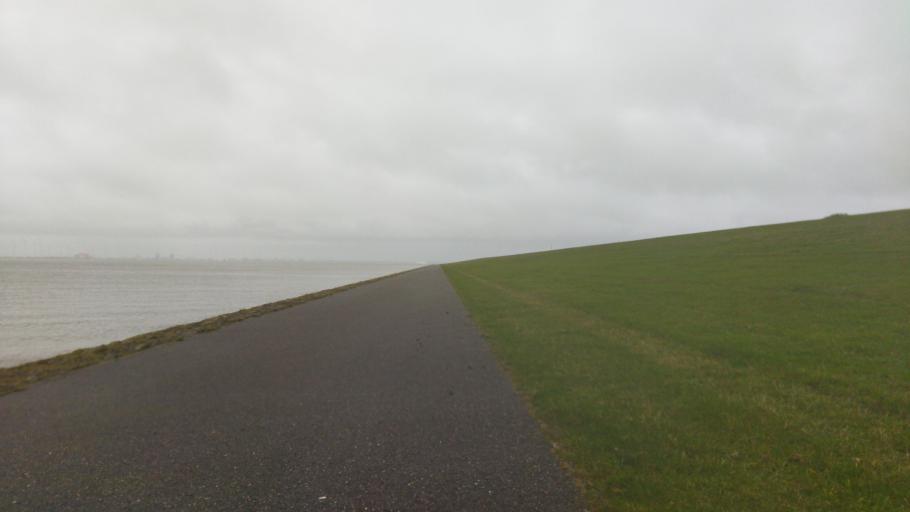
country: DE
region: Lower Saxony
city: Hinte
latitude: 53.3347
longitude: 7.0691
